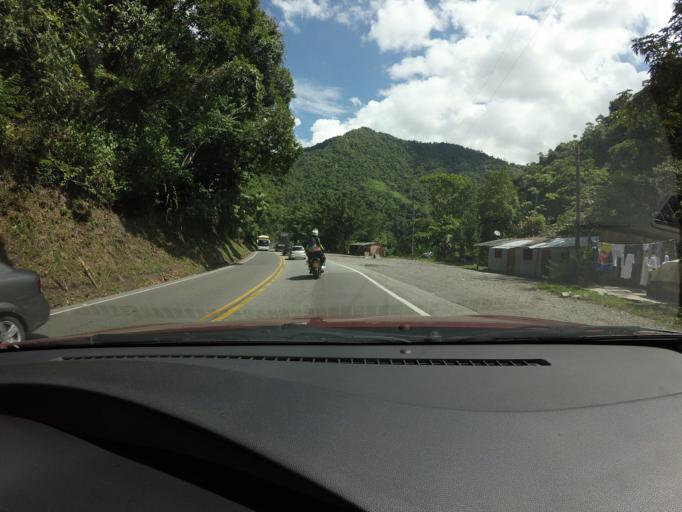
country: CO
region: Antioquia
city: San Luis
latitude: 5.9997
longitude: -74.9416
